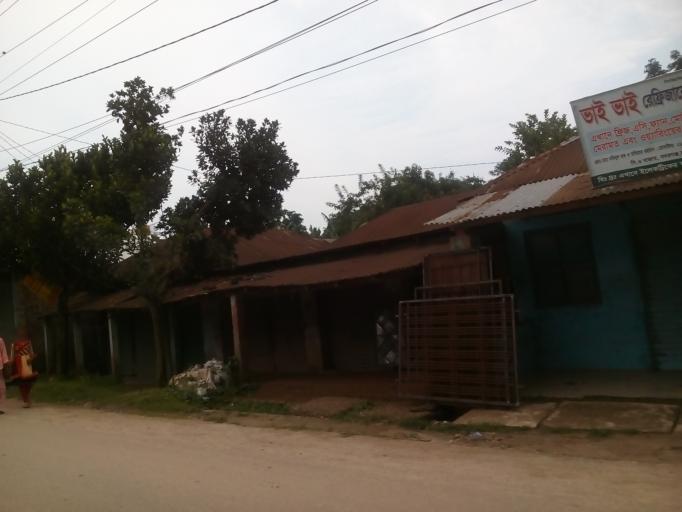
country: BD
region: Rangpur Division
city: Badarganj
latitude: 25.6686
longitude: 89.0498
